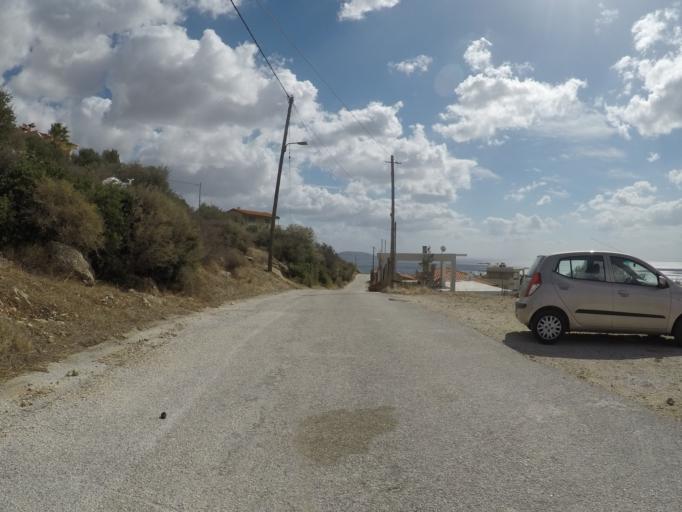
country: GR
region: Attica
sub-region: Nomarchia Anatolikis Attikis
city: Agios Dimitrios Kropias
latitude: 37.8000
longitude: 23.8784
